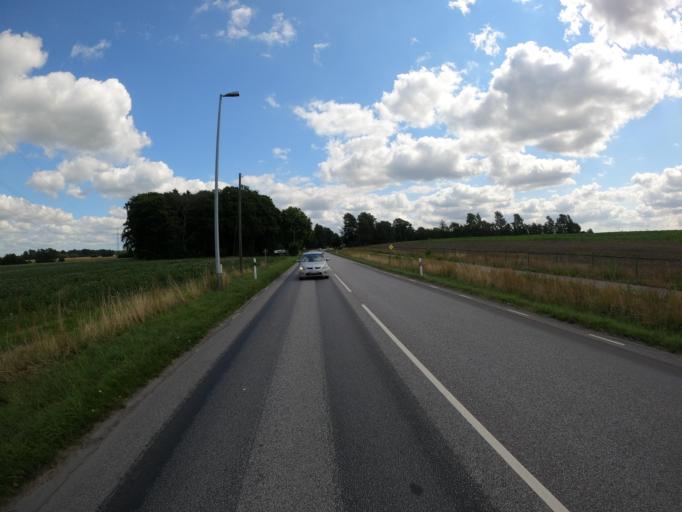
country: SE
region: Skane
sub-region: Lunds Kommun
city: Veberod
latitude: 55.6434
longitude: 13.4757
